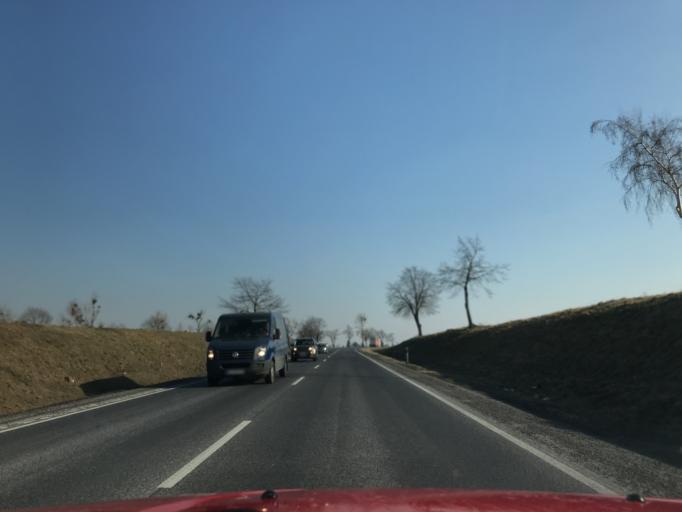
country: PL
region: Greater Poland Voivodeship
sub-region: Powiat sredzki
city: Nowe Miasto nad Warta
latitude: 52.0807
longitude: 17.4111
